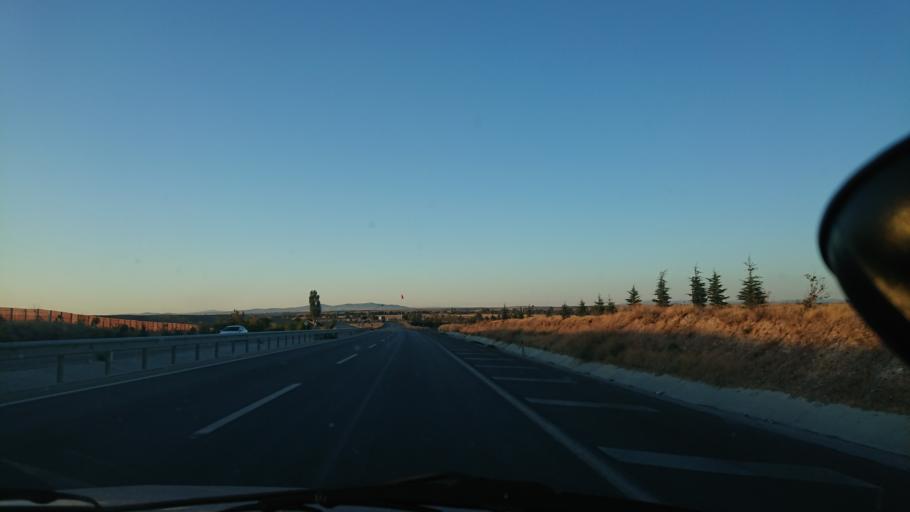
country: TR
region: Eskisehir
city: Mahmudiye
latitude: 39.5139
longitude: 30.9639
